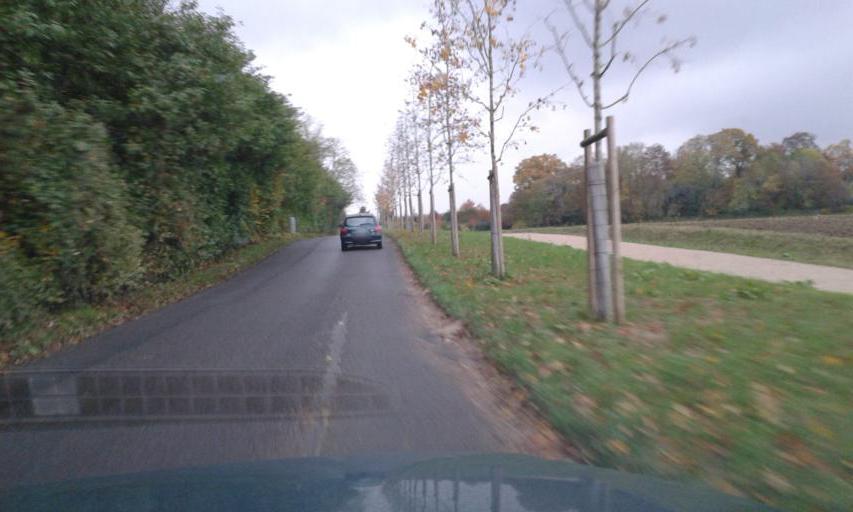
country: FR
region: Centre
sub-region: Departement du Loiret
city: Olivet
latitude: 47.8710
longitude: 1.8865
